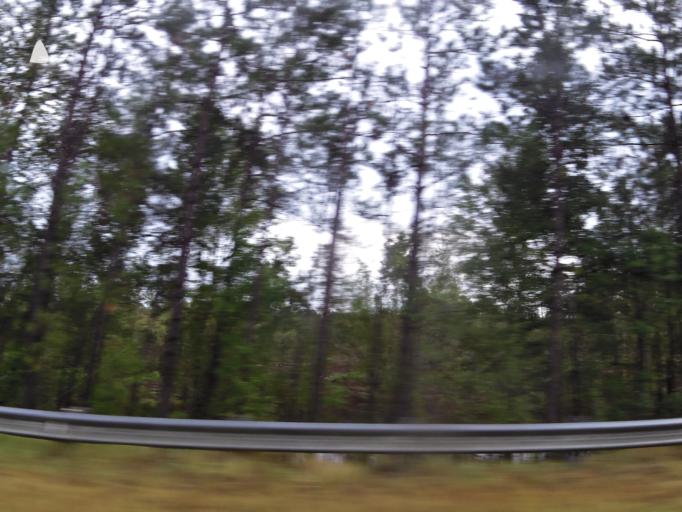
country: US
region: Georgia
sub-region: Long County
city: Ludowici
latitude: 31.6985
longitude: -81.7732
